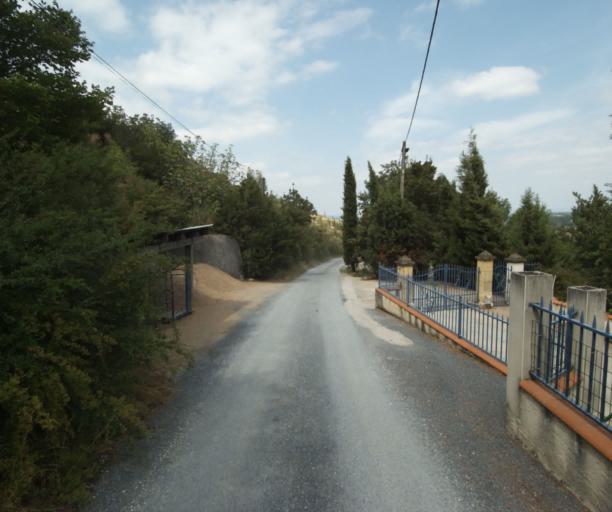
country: FR
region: Midi-Pyrenees
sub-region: Departement du Tarn
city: Soreze
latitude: 43.4443
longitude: 2.0448
